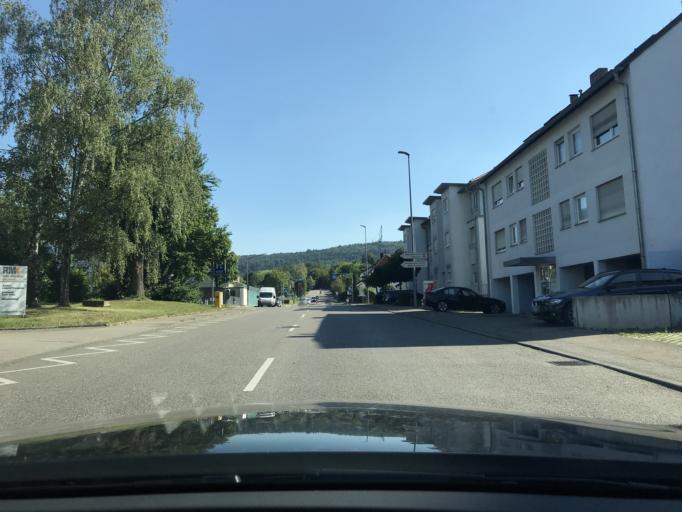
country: DE
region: Baden-Wuerttemberg
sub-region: Regierungsbezirk Stuttgart
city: Schorndorf
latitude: 48.7984
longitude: 9.5279
